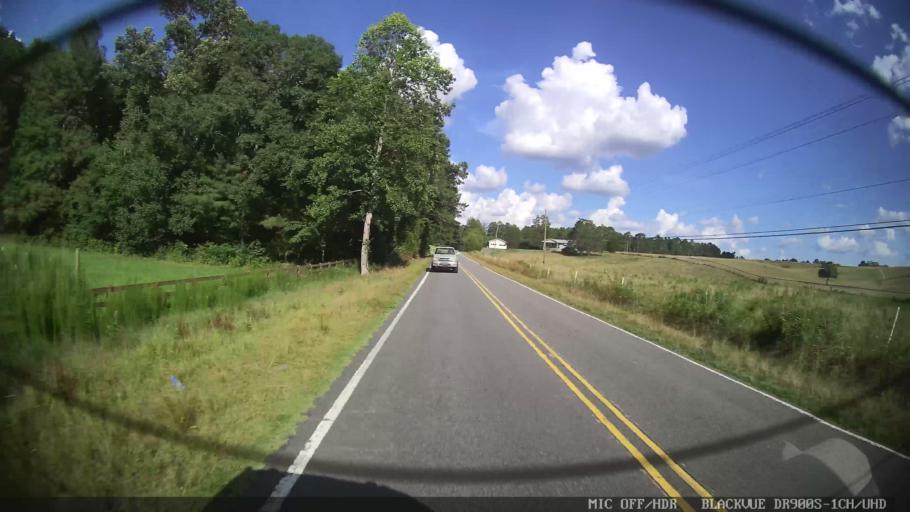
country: US
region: Georgia
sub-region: Floyd County
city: Lindale
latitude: 34.1961
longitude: -85.0780
